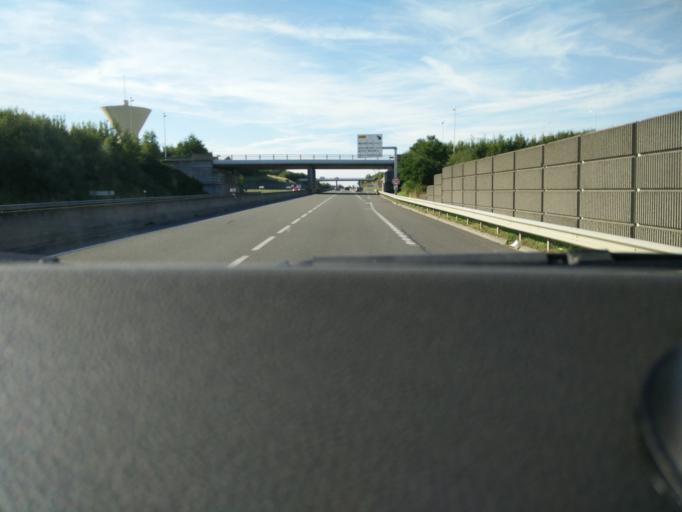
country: FR
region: Nord-Pas-de-Calais
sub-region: Departement du Nord
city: Hautmont
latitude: 50.2654
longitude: 3.9247
